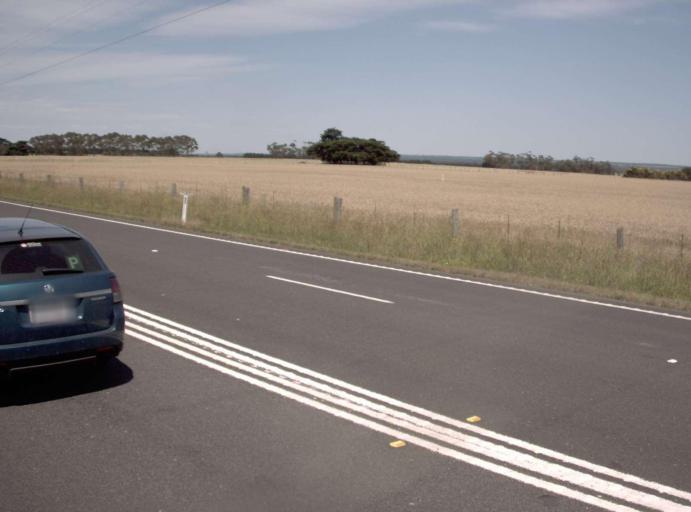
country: AU
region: Victoria
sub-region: Wellington
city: Sale
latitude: -38.1023
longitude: 146.9420
